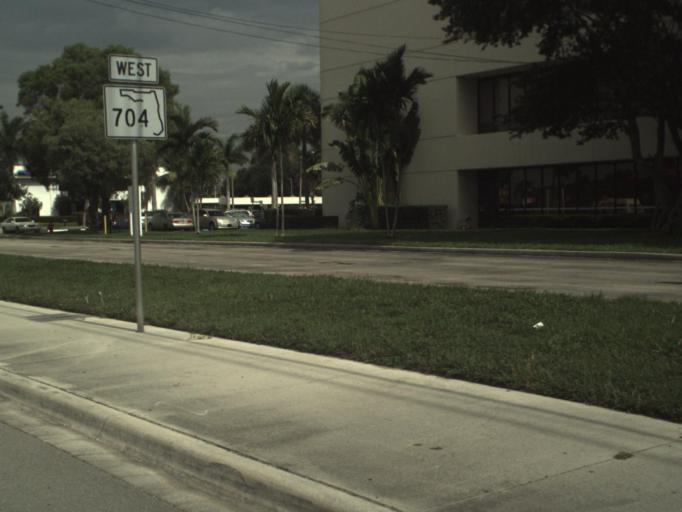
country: US
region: Florida
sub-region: Palm Beach County
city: Plantation Mobile Home Park
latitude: 26.7075
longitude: -80.1326
